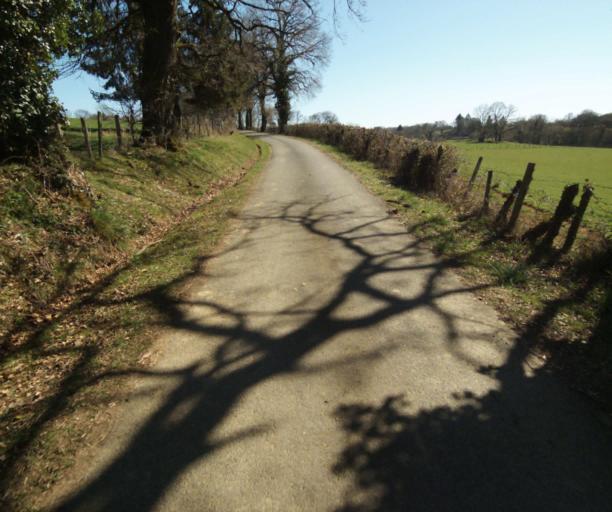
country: FR
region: Limousin
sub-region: Departement de la Correze
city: Seilhac
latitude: 45.3871
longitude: 1.6760
